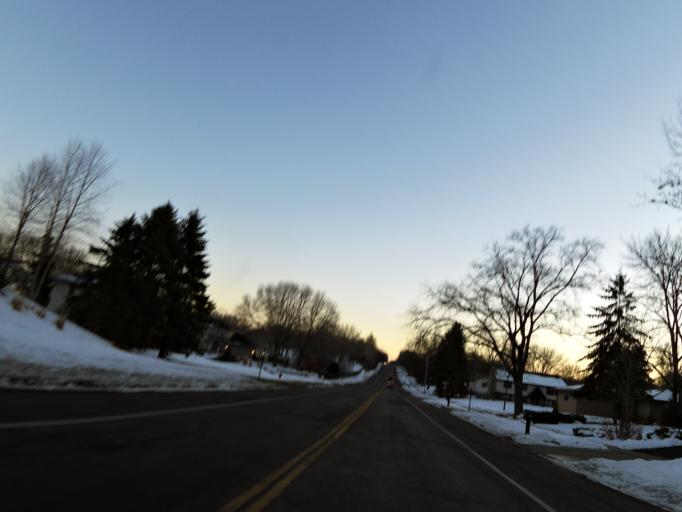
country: US
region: Minnesota
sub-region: Scott County
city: Savage
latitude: 44.8243
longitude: -93.3585
